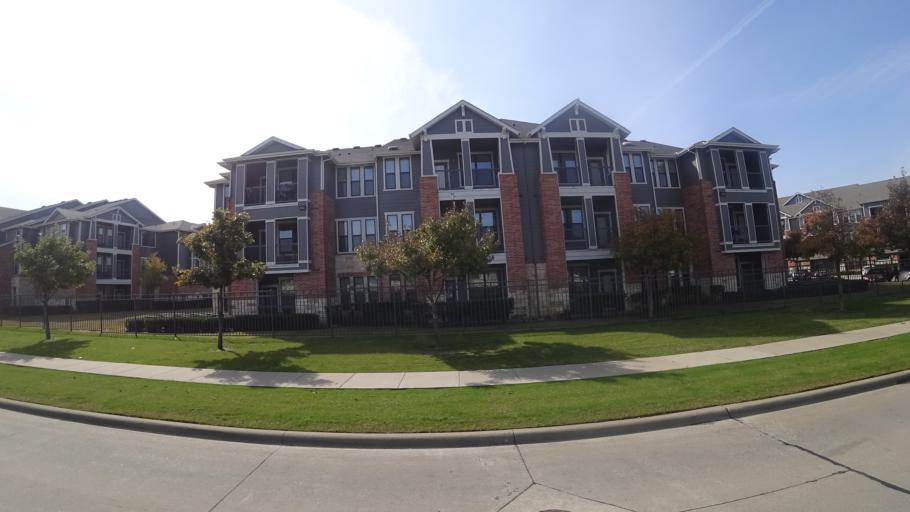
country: US
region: Texas
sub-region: Denton County
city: The Colony
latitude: 33.0626
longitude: -96.8791
